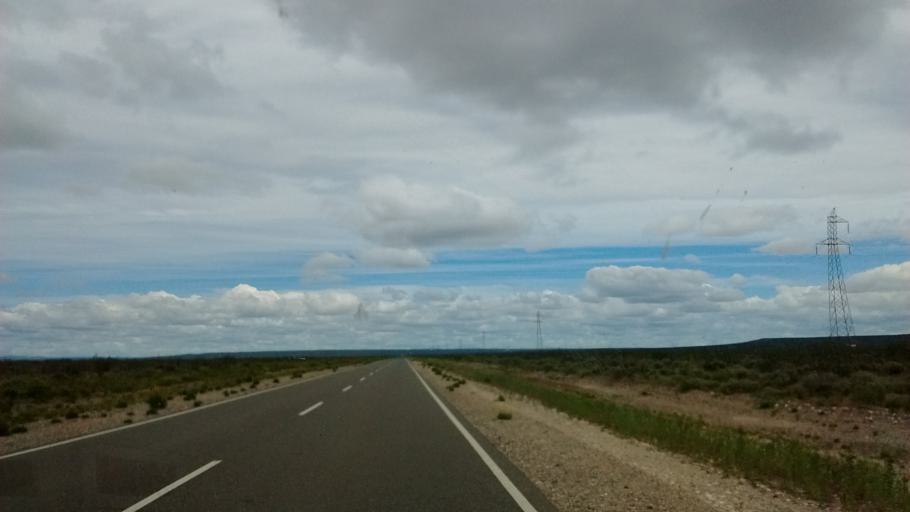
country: AR
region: Neuquen
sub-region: Departamento de Picun Leufu
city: Picun Leufu
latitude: -39.6731
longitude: -69.4475
